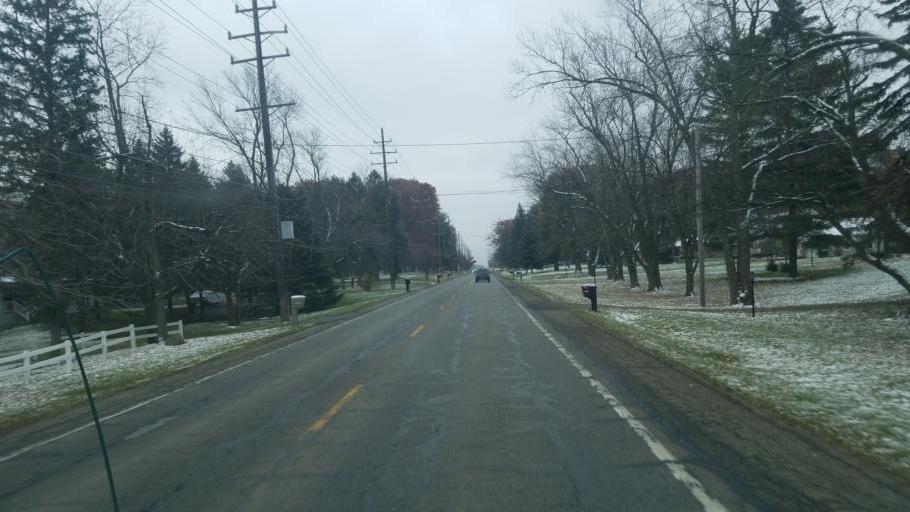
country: US
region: Ohio
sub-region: Summit County
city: Northfield
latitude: 41.3581
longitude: -81.5386
